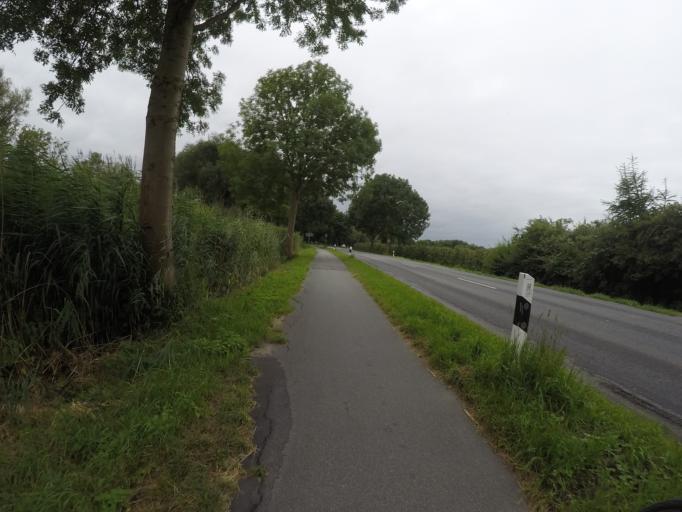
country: DE
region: Schleswig-Holstein
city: Wedel
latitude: 53.5425
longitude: 9.7366
